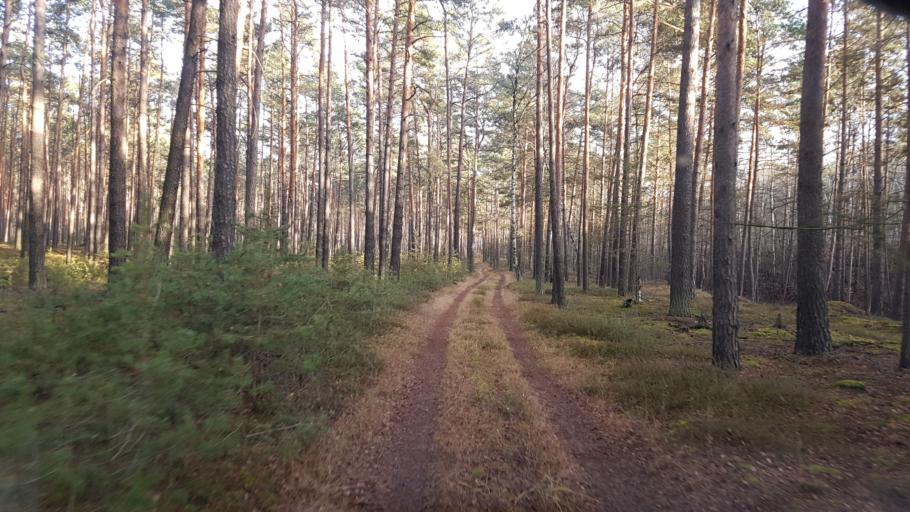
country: DE
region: Brandenburg
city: Finsterwalde
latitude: 51.6284
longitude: 13.6573
